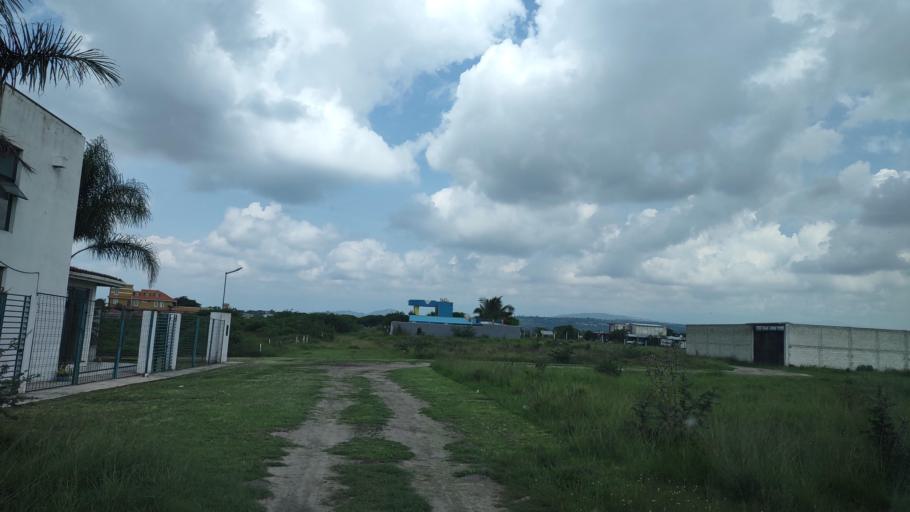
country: MX
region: Veracruz
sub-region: Emiliano Zapata
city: Dos Rios
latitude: 19.4623
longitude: -96.7916
